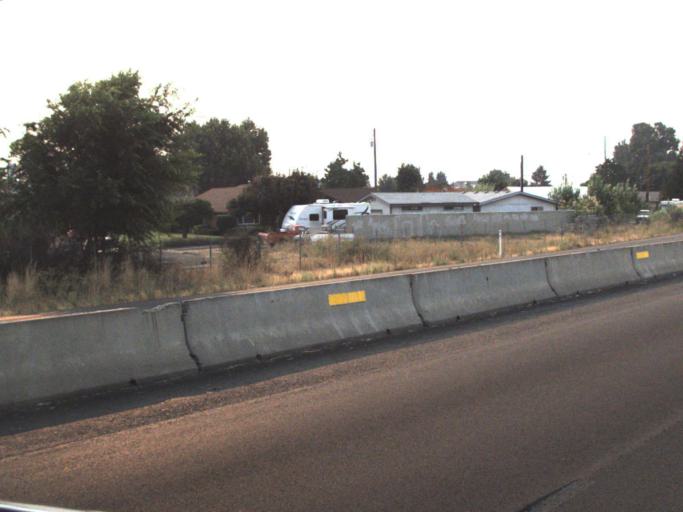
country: US
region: Washington
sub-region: Yakima County
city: Wapato
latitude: 46.4416
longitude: -120.4292
